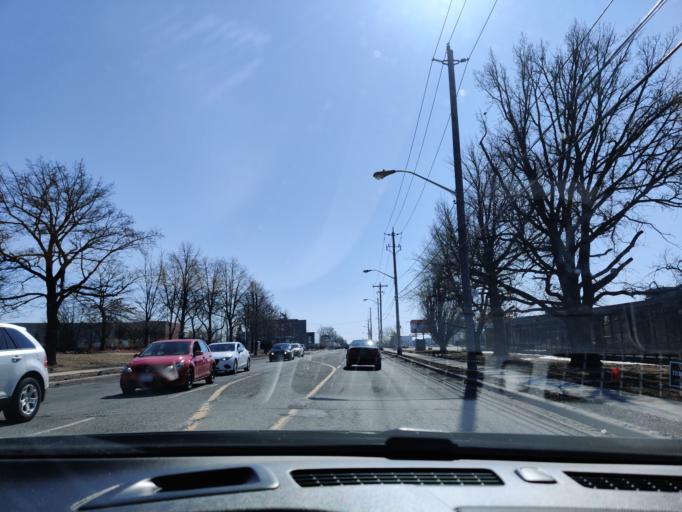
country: CA
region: Ontario
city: Toronto
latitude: 43.7015
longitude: -79.4642
